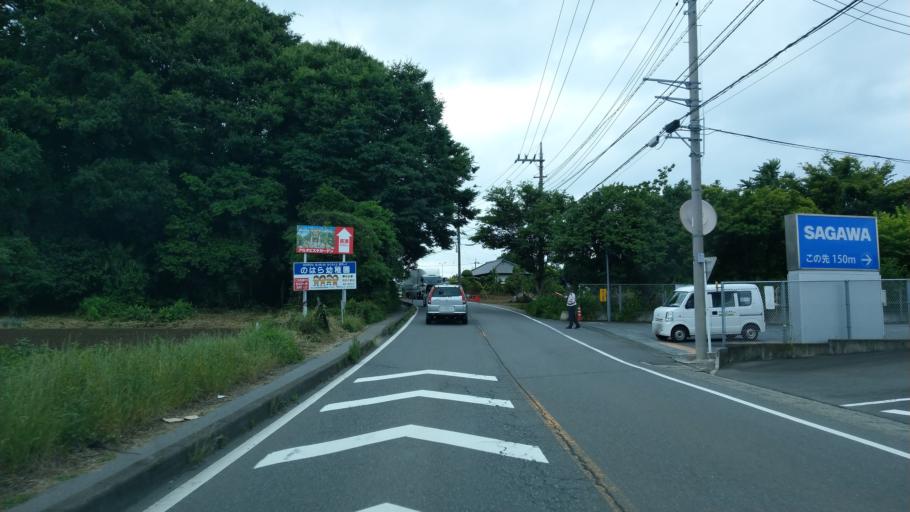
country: JP
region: Saitama
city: Ageoshimo
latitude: 35.9257
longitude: 139.5953
